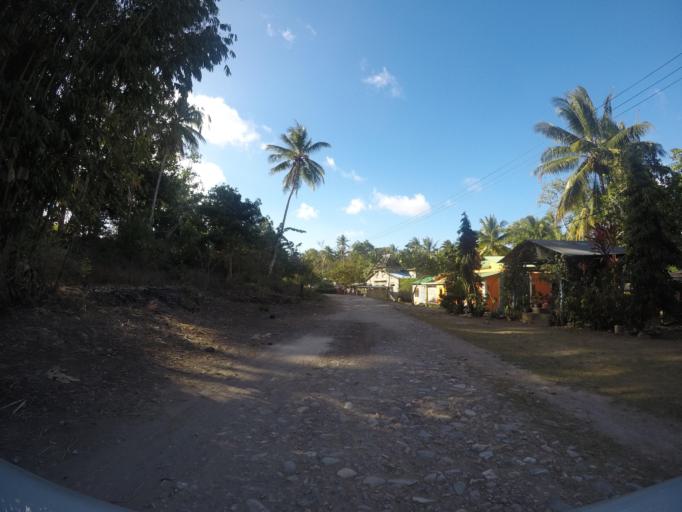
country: TL
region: Lautem
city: Lospalos
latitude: -8.4502
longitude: 126.8817
